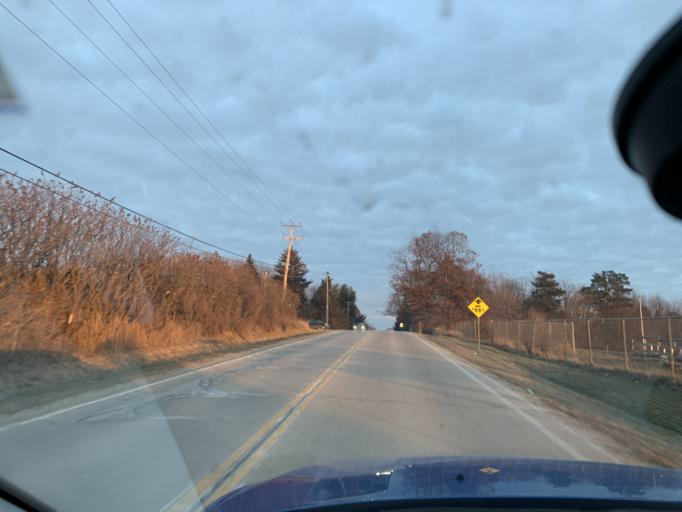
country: US
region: Wisconsin
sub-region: Dane County
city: Verona
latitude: 43.0457
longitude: -89.5534
